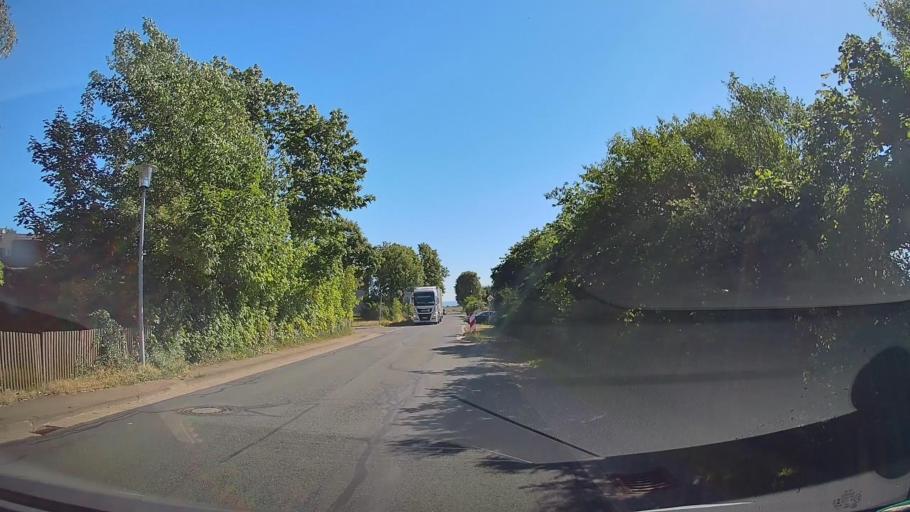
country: DE
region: Lower Saxony
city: Vahlbruch
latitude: 51.9618
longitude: 9.3337
